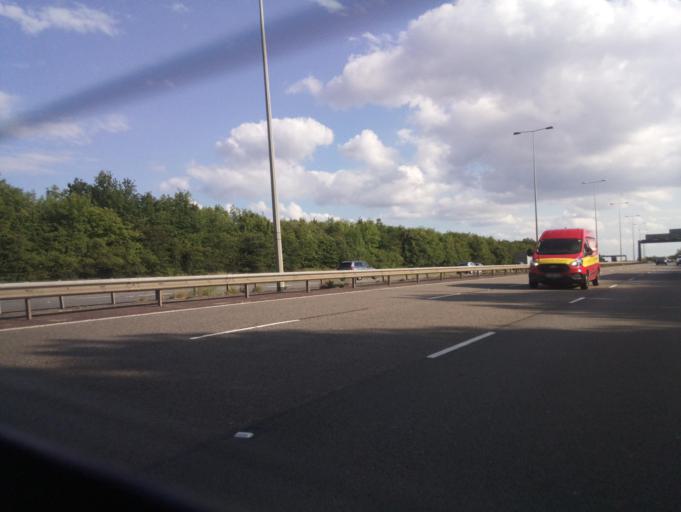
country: GB
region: England
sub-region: Cambridgeshire
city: Stilton
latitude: 52.4843
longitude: -0.2864
